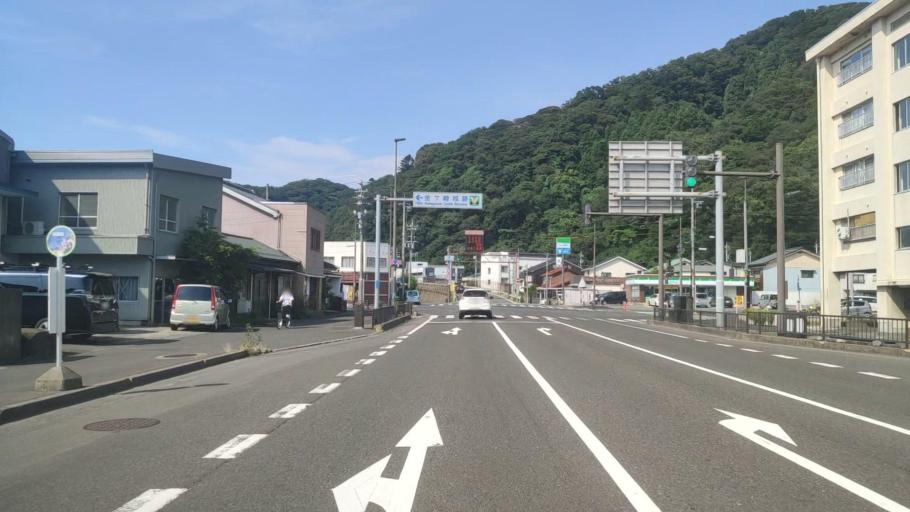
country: JP
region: Fukui
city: Tsuruga
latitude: 35.6579
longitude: 136.0760
